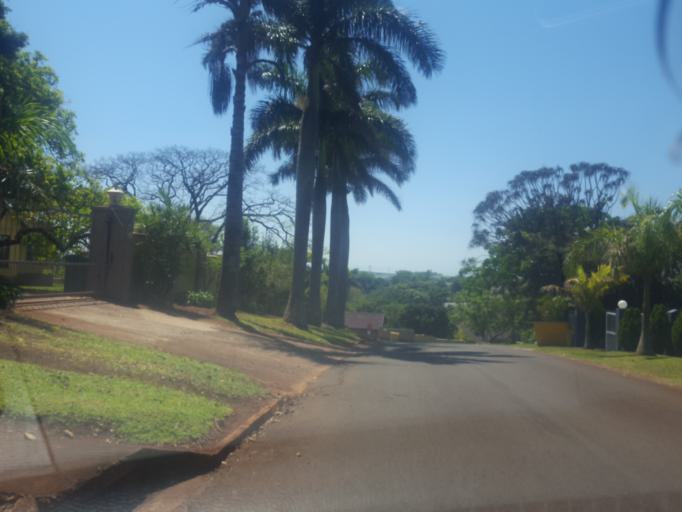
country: ZA
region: KwaZulu-Natal
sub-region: uThungulu District Municipality
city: Empangeni
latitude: -28.7467
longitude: 31.9013
